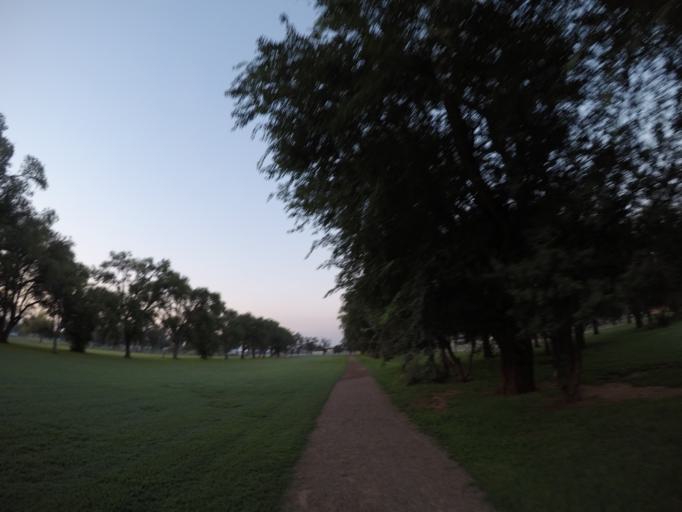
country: US
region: New Mexico
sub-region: Curry County
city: Clovis
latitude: 34.4068
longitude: -103.1864
